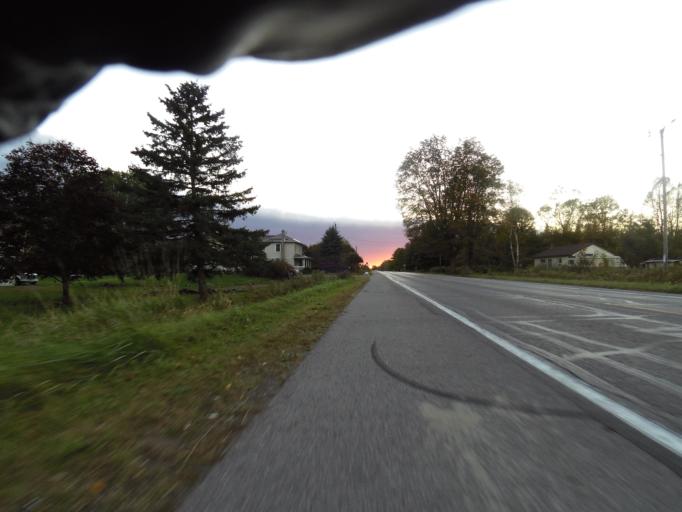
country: CA
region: Ontario
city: Quinte West
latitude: 44.0402
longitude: -77.6809
